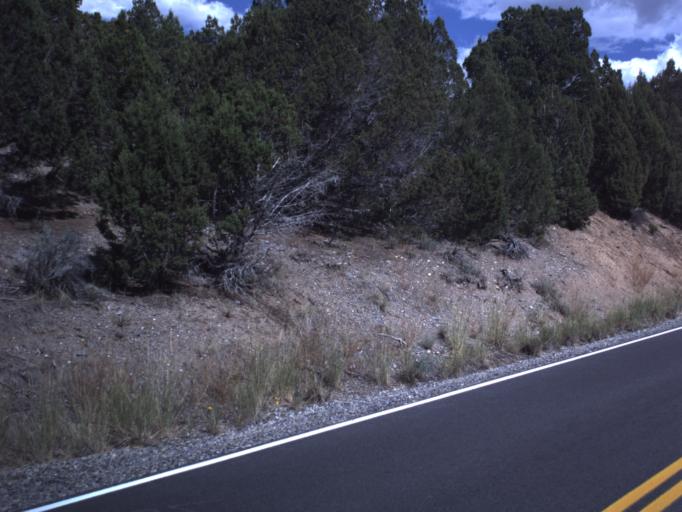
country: US
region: Utah
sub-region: Tooele County
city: Grantsville
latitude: 40.3446
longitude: -112.5838
